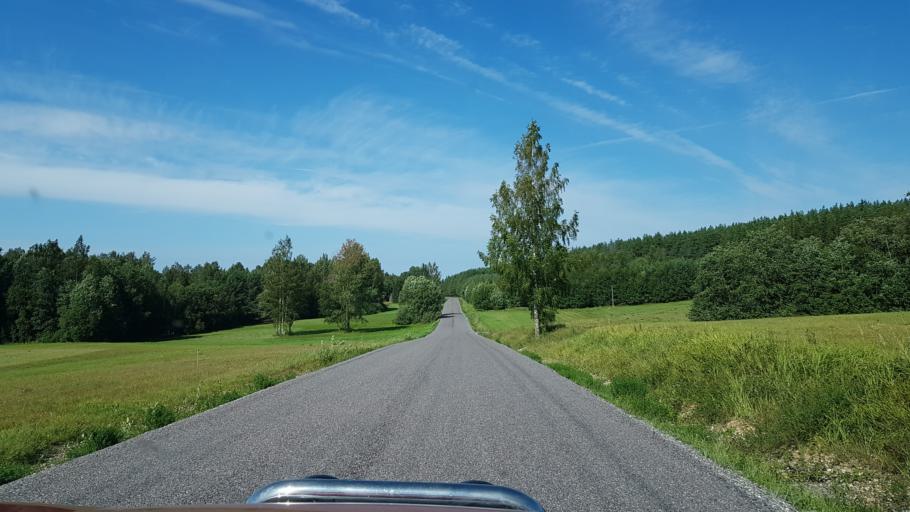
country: EE
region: Tartu
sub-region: Elva linn
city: Elva
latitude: 58.2457
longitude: 26.3844
